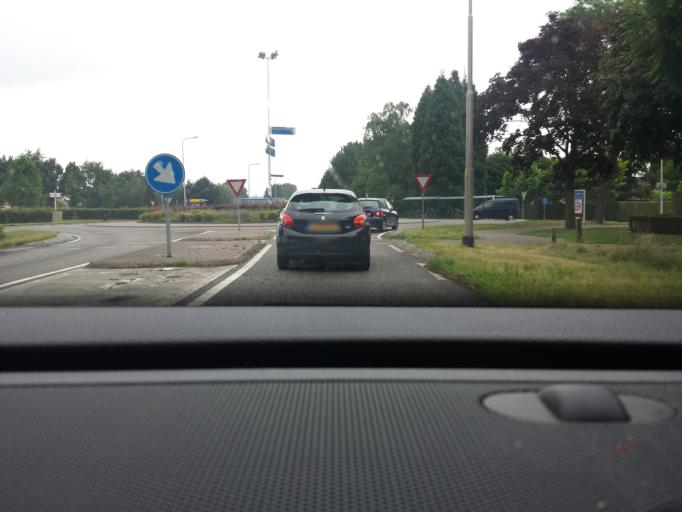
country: NL
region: Gelderland
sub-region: Gemeente Bronckhorst
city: Hengelo
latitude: 52.0498
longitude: 6.3055
